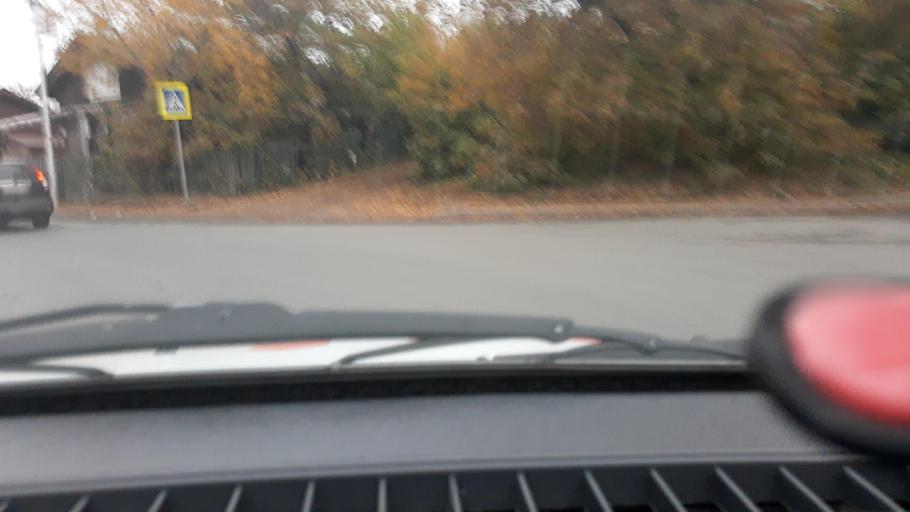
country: RU
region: Bashkortostan
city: Ufa
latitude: 54.7526
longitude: 55.9634
